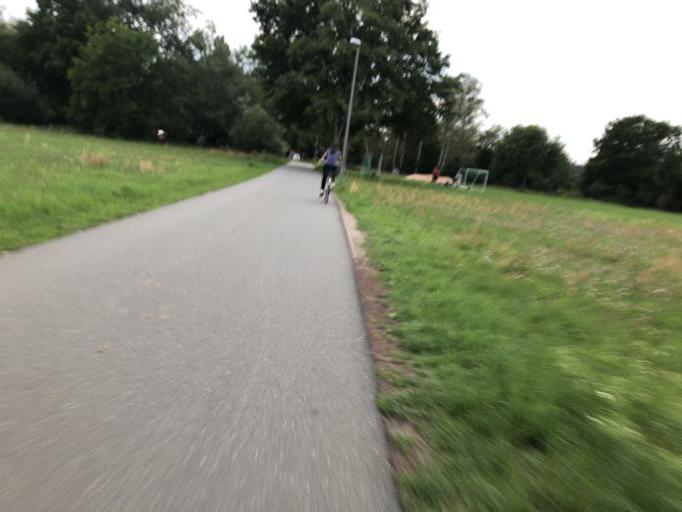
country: DE
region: Bavaria
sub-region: Regierungsbezirk Mittelfranken
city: Erlangen
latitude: 49.5940
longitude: 10.9818
